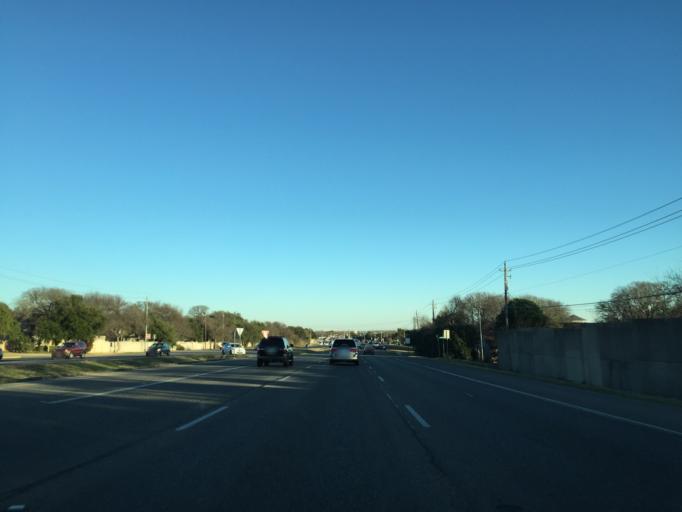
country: US
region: Texas
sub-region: Travis County
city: Wells Branch
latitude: 30.4273
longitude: -97.7190
